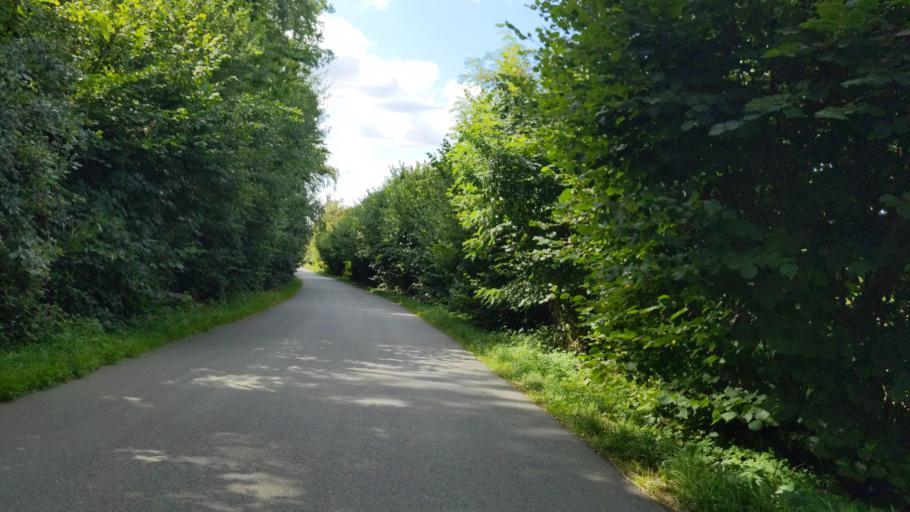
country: DE
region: Schleswig-Holstein
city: Susel
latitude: 54.1152
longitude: 10.7225
